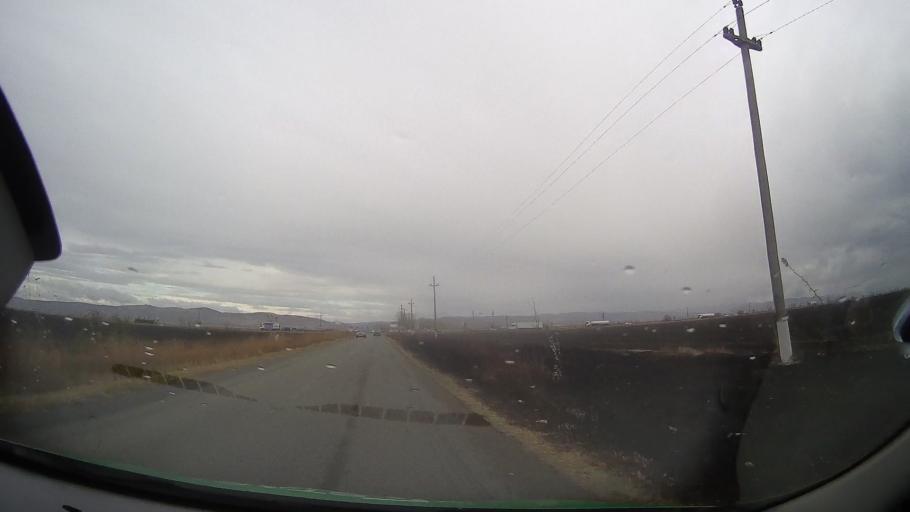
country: RO
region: Prahova
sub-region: Comuna Colceag
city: Inotesti
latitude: 44.9772
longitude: 26.3410
